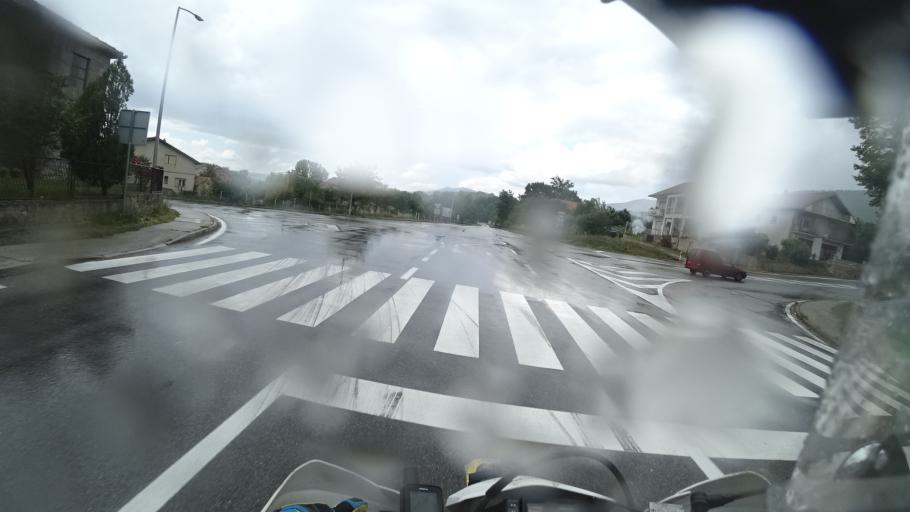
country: HR
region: Sibensko-Kniniska
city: Knin
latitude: 44.0425
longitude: 16.2259
